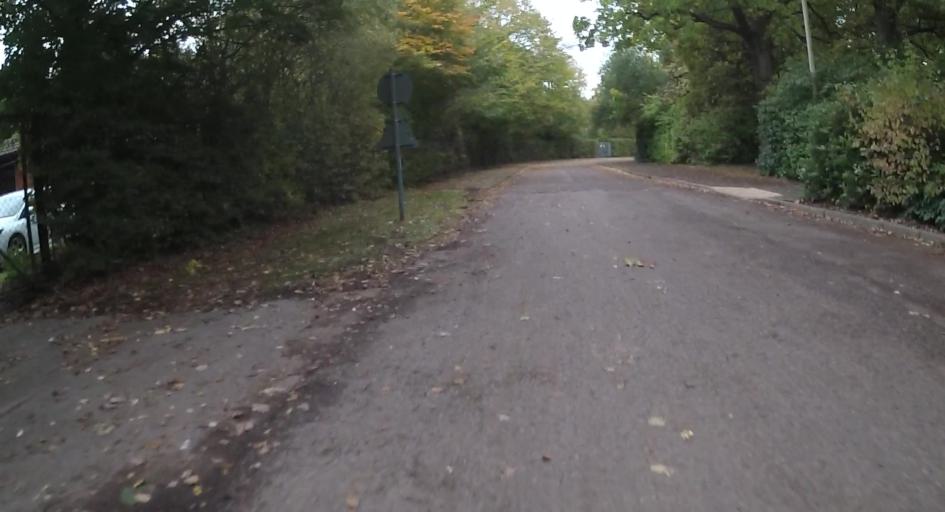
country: GB
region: England
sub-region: Bracknell Forest
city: Crowthorne
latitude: 51.3998
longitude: -0.7841
